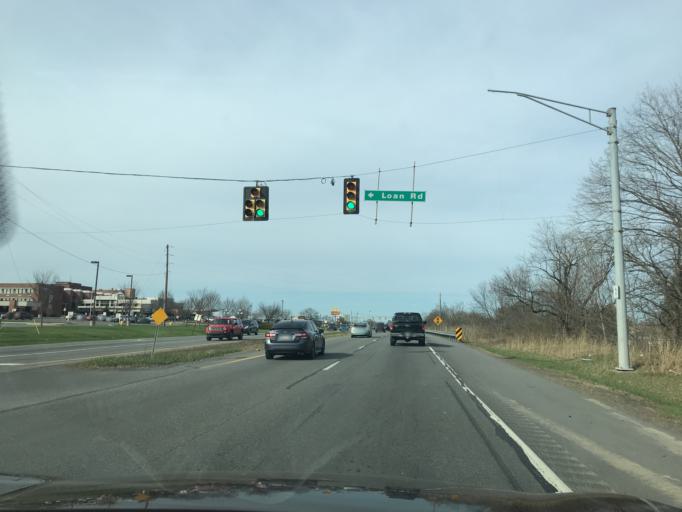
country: US
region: Pennsylvania
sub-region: Union County
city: Lewisburg
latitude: 40.9772
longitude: -76.8868
